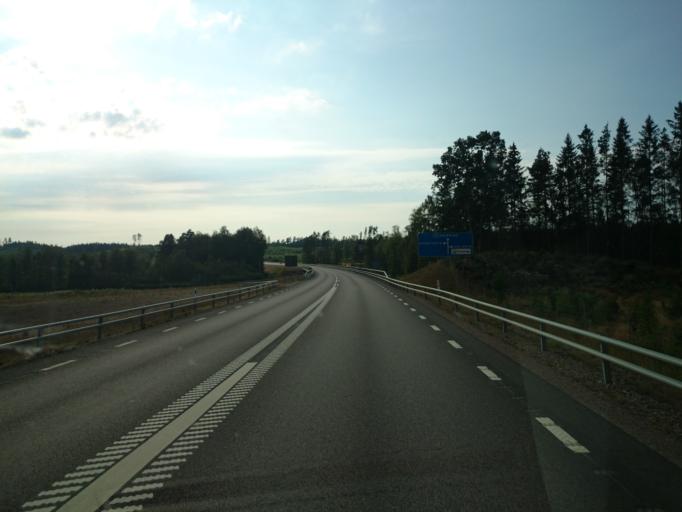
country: SE
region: Skane
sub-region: Osby Kommun
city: Osby
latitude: 56.4321
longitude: 13.8724
